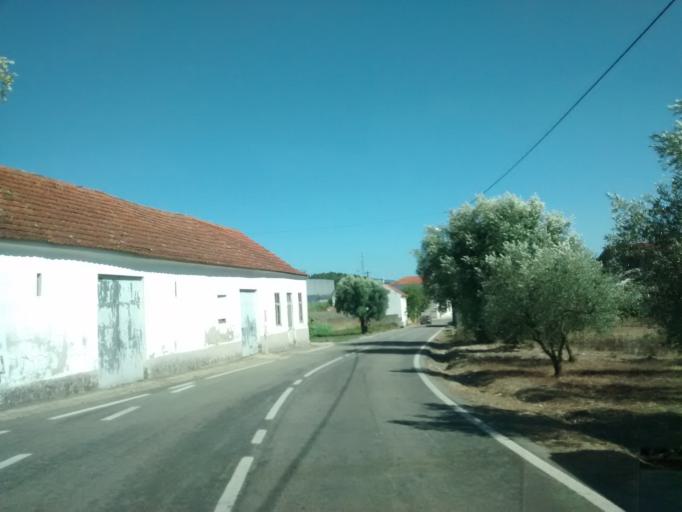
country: PT
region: Aveiro
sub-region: Anadia
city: Sangalhos
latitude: 40.4399
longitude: -8.5001
